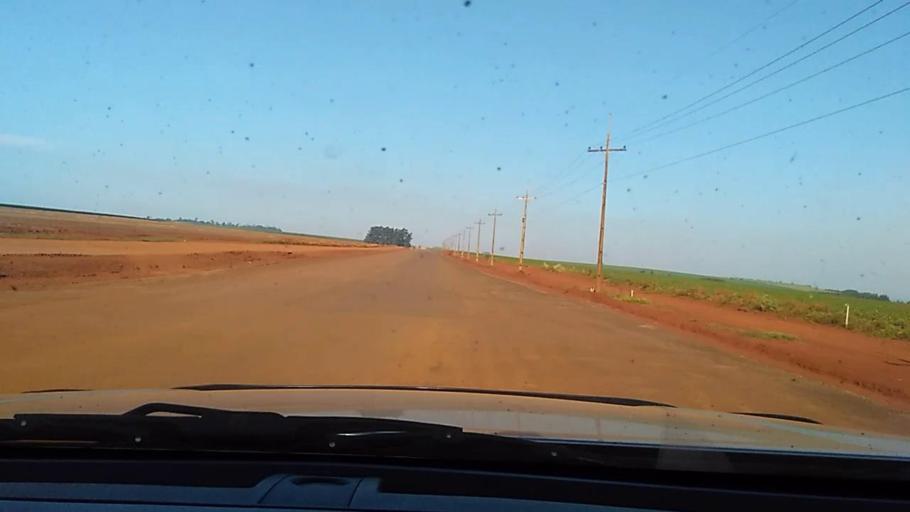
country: PY
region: Alto Parana
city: Naranjal
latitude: -25.9165
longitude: -55.4356
